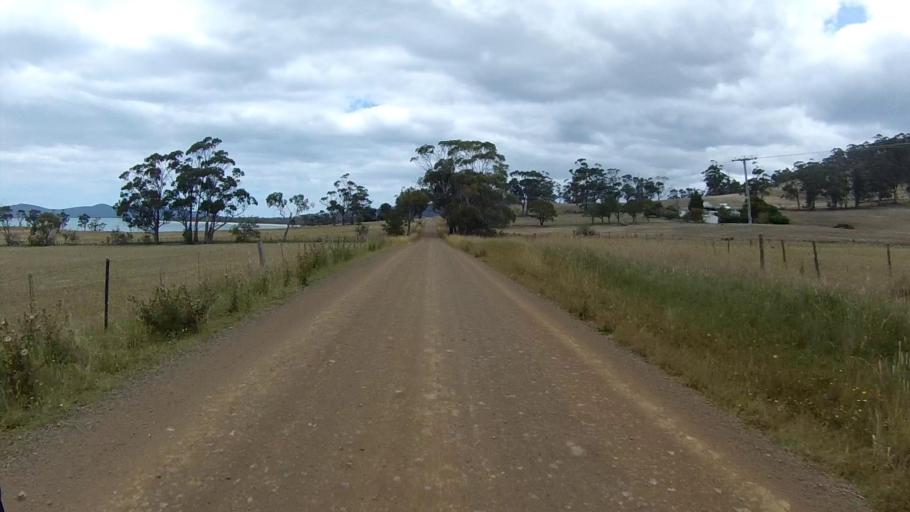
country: AU
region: Tasmania
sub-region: Sorell
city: Sorell
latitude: -42.6220
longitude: 147.9326
